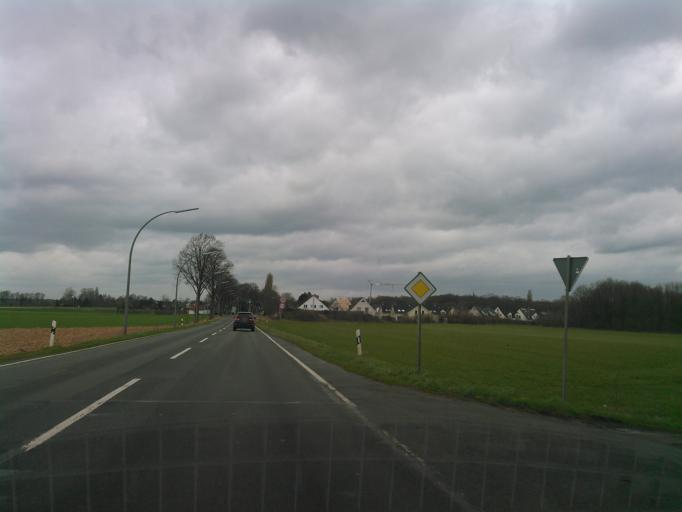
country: DE
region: North Rhine-Westphalia
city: Marl
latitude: 51.6368
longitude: 7.0823
